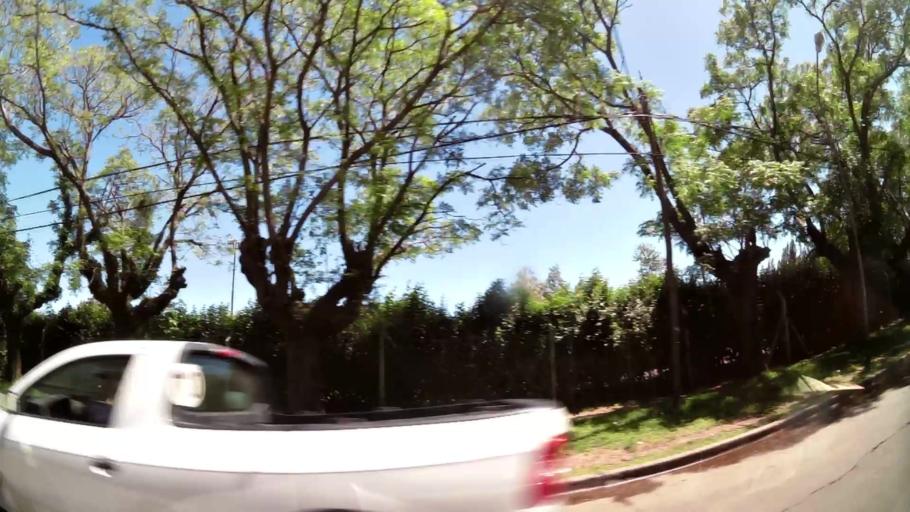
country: AR
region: Buenos Aires
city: Hurlingham
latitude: -34.4971
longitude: -58.6417
